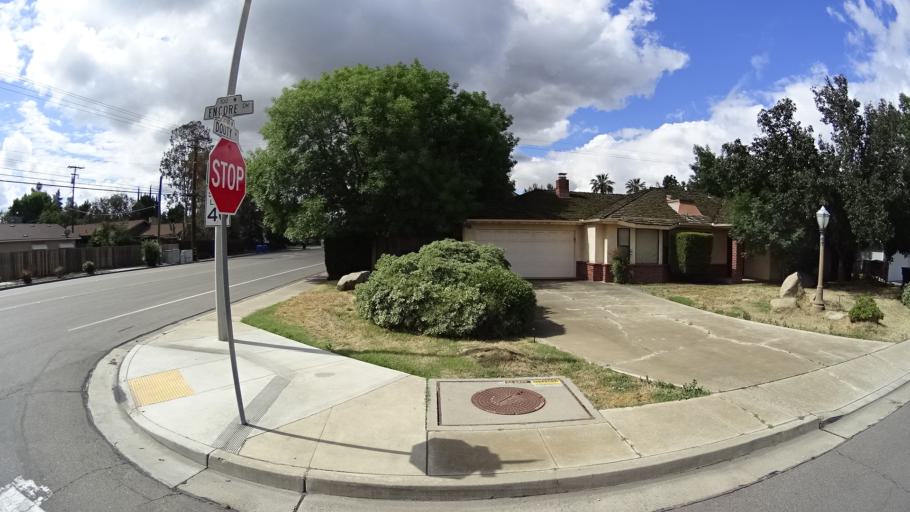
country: US
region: California
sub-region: Kings County
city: Lucerne
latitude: 36.3613
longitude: -119.6462
